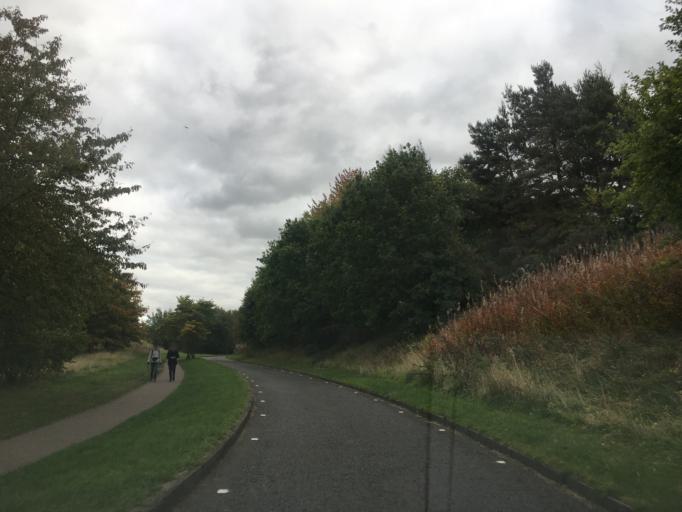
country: GB
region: Scotland
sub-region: West Lothian
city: Seafield
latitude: 55.9534
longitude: -3.1552
